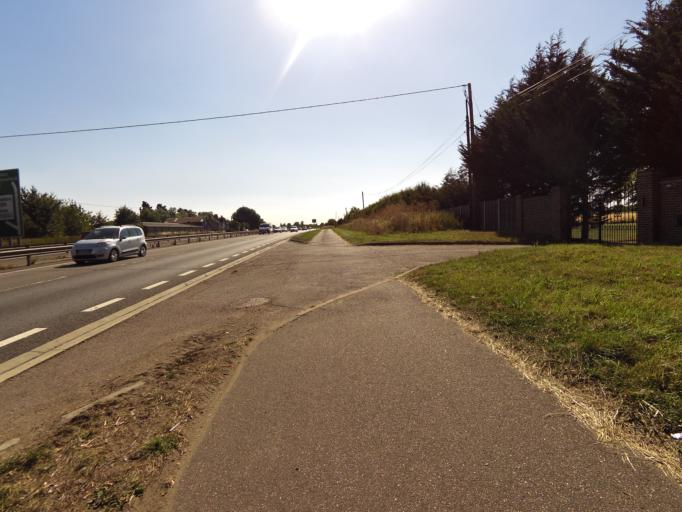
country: GB
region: England
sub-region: Essex
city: Kelvedon
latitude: 51.8516
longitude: 0.7298
